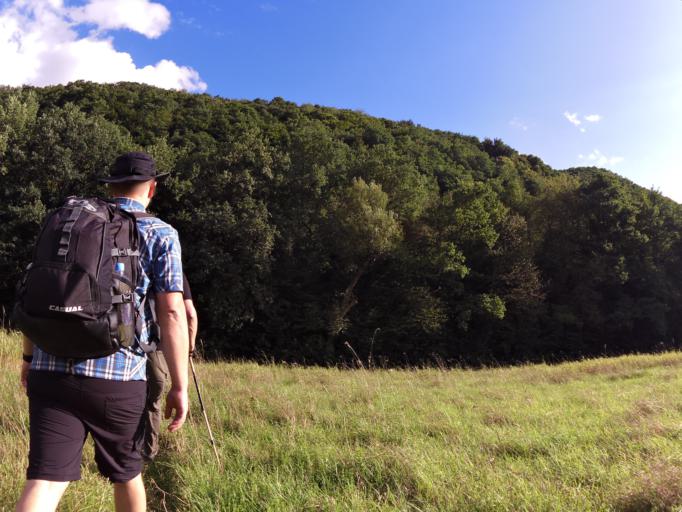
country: DE
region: Rheinland-Pfalz
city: Norheim
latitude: 49.8051
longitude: 7.8150
